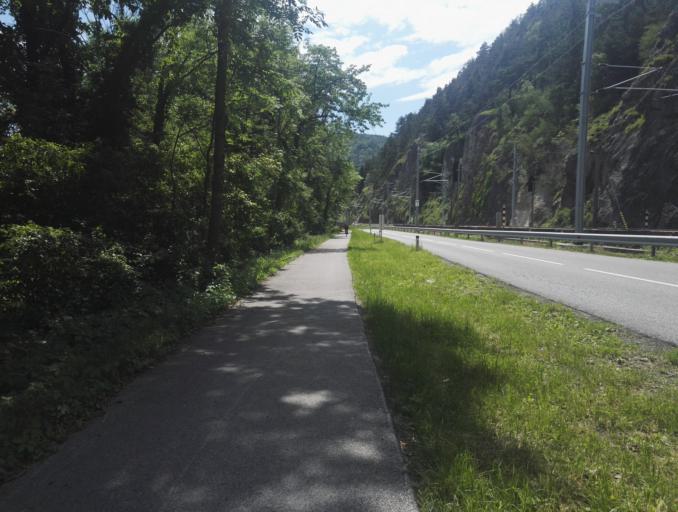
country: AT
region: Styria
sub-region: Politischer Bezirk Graz-Umgebung
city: Deutschfeistritz
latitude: 47.1652
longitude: 15.3183
